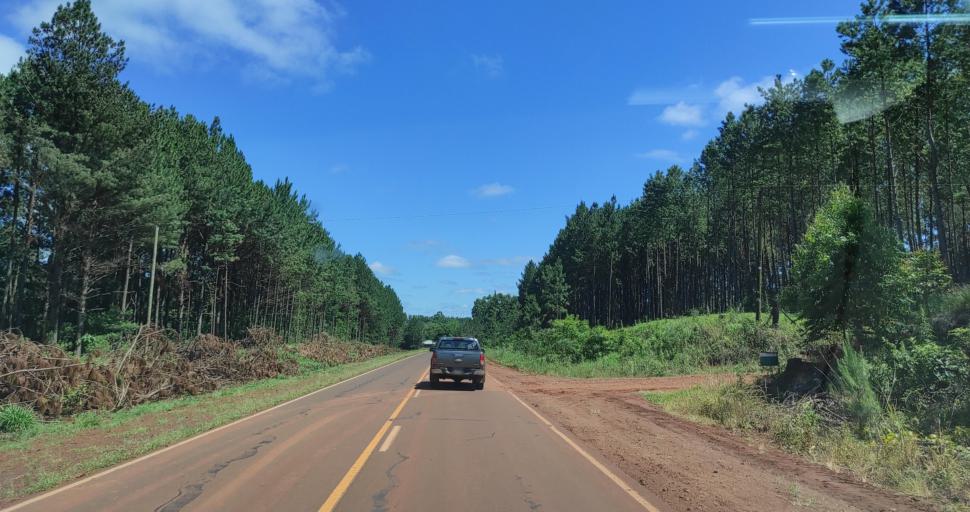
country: AR
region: Misiones
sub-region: Departamento de Veinticinco de Mayo
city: Veinticinco de Mayo
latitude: -27.4150
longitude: -54.7376
